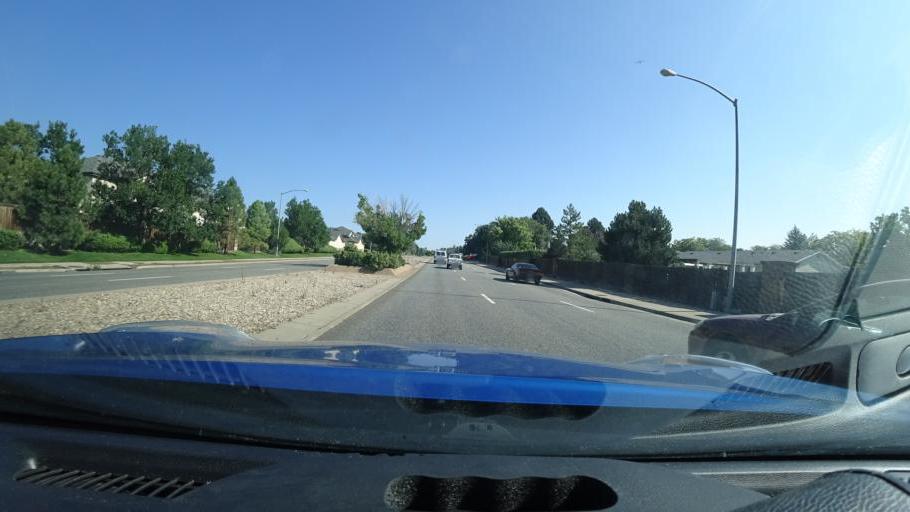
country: US
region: Colorado
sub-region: Adams County
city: Aurora
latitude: 39.6901
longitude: -104.8098
